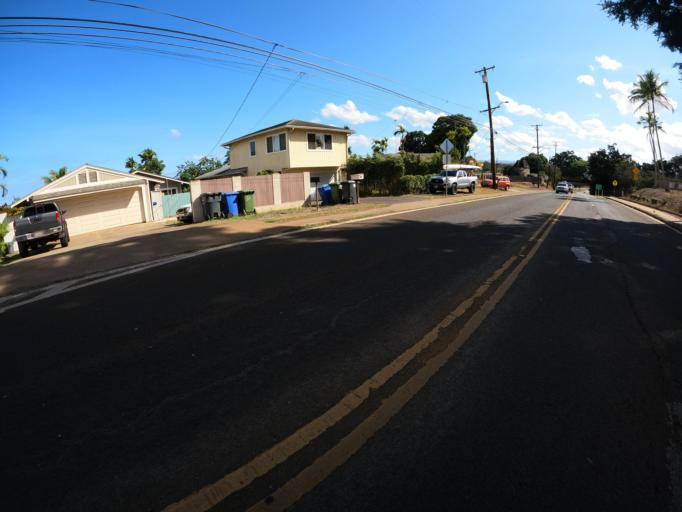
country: US
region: Hawaii
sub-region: Honolulu County
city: Waialua
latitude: 21.5668
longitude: -158.1249
